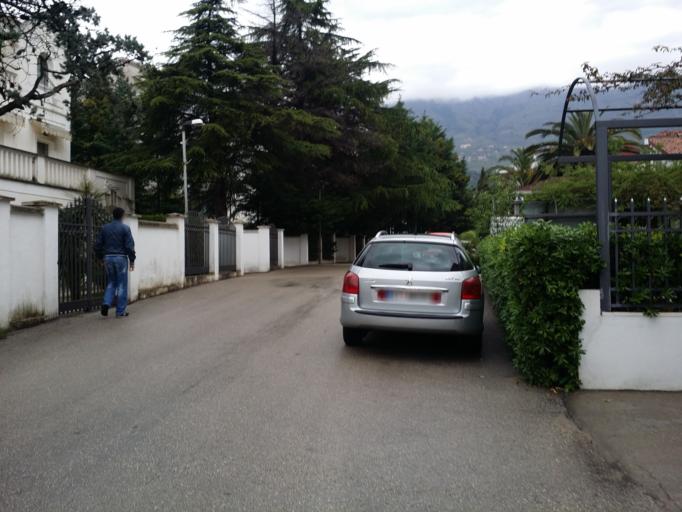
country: ME
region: Budva
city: Budva
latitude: 42.2866
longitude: 18.8399
